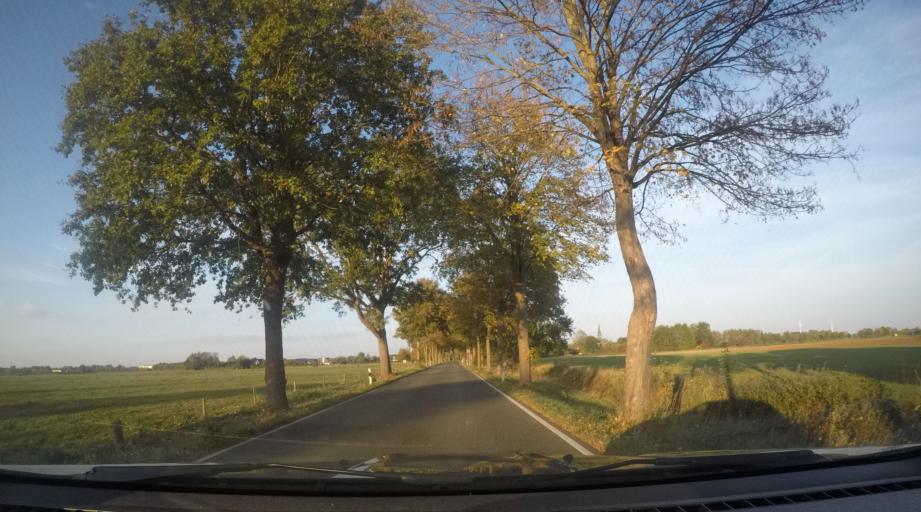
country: DE
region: North Rhine-Westphalia
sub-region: Regierungsbezirk Munster
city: Isselburg
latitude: 51.8148
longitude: 6.5042
